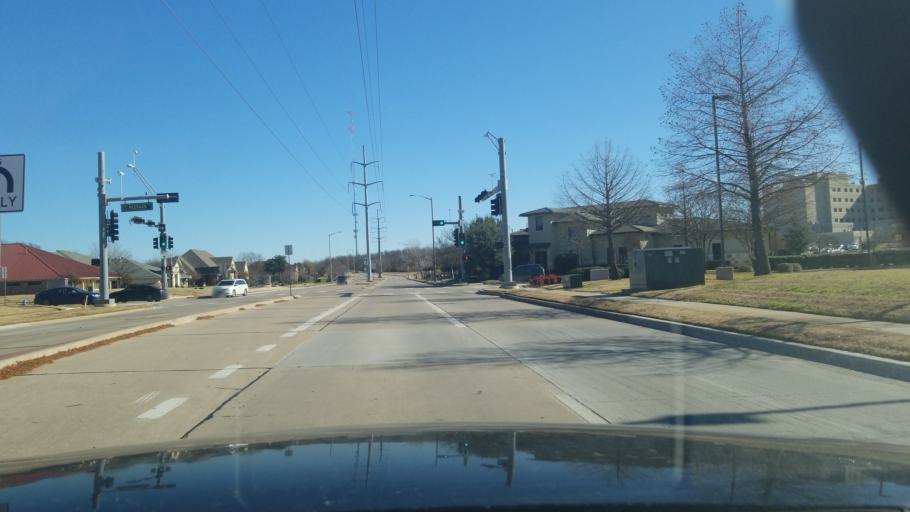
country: US
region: Texas
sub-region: Denton County
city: Corinth
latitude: 33.1807
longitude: -97.0935
